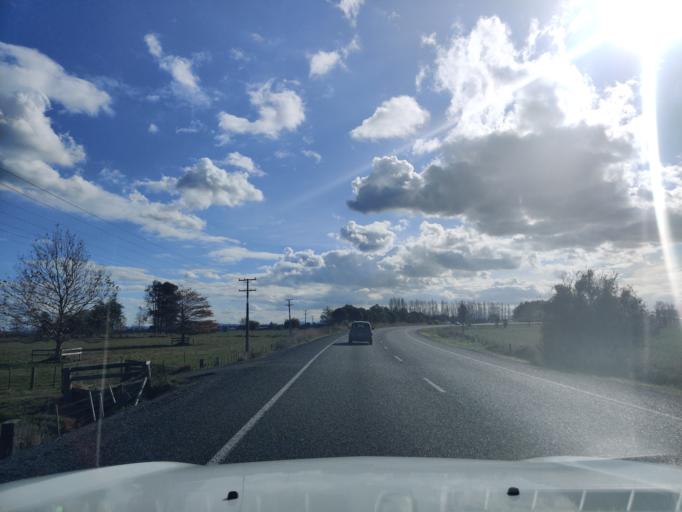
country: NZ
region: Waikato
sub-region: Hauraki District
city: Ngatea
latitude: -37.2808
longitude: 175.5371
